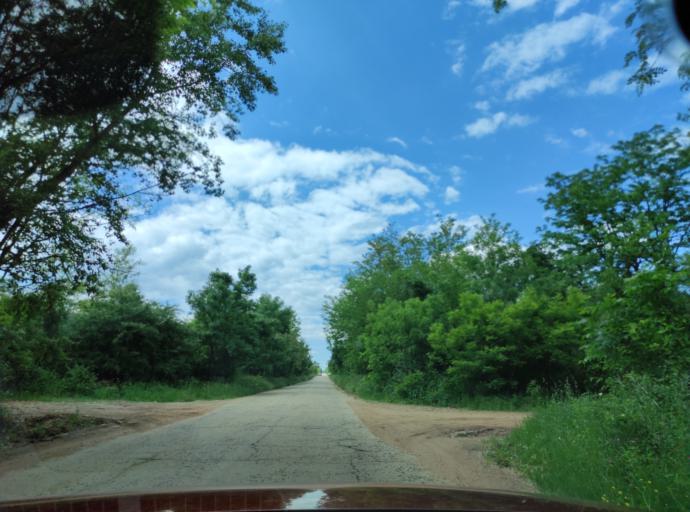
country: BG
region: Montana
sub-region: Obshtina Berkovitsa
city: Berkovitsa
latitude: 43.3599
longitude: 23.0915
